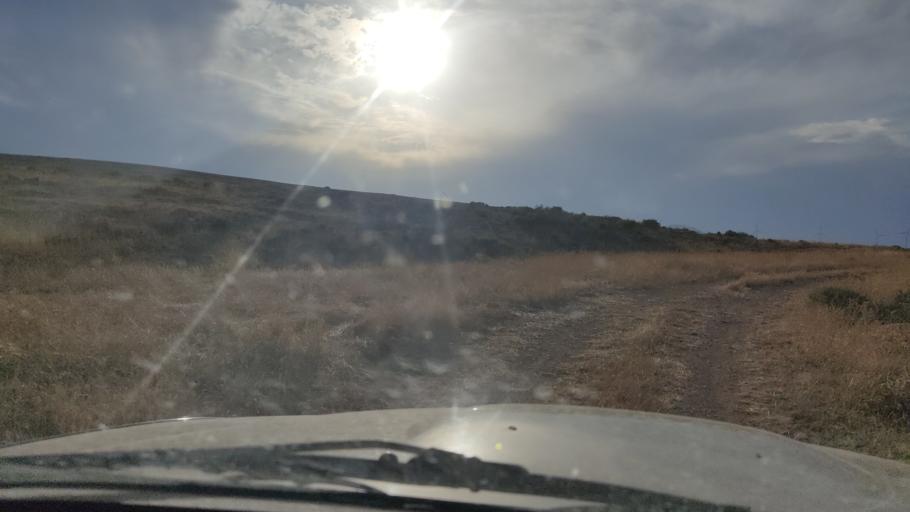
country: ES
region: Aragon
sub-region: Provincia de Teruel
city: Monforte de Moyuela
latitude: 41.0591
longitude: -0.9751
